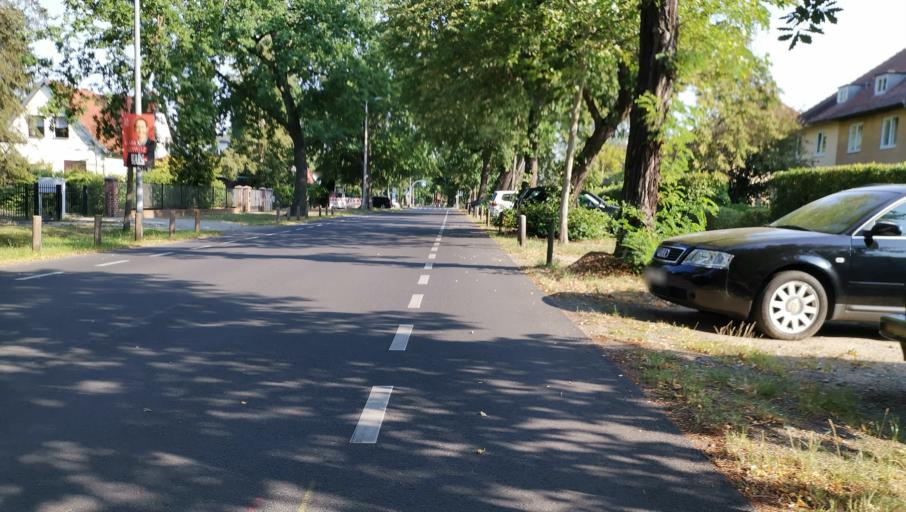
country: DE
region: Brandenburg
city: Potsdam
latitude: 52.3869
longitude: 13.0129
